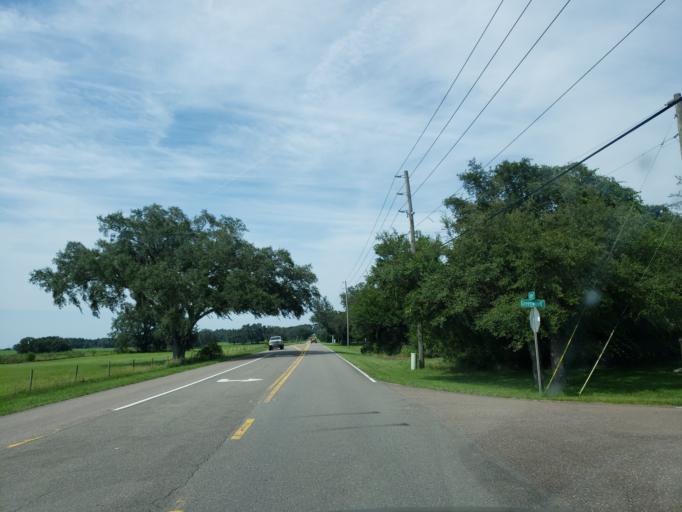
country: US
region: Florida
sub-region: Pasco County
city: San Antonio
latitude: 28.2946
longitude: -82.2787
